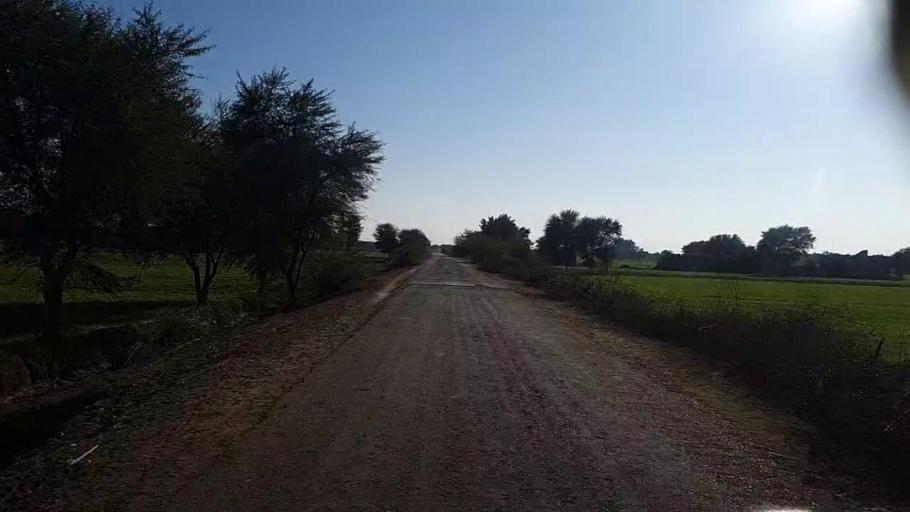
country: PK
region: Sindh
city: Khairpur
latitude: 27.8955
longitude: 69.7469
